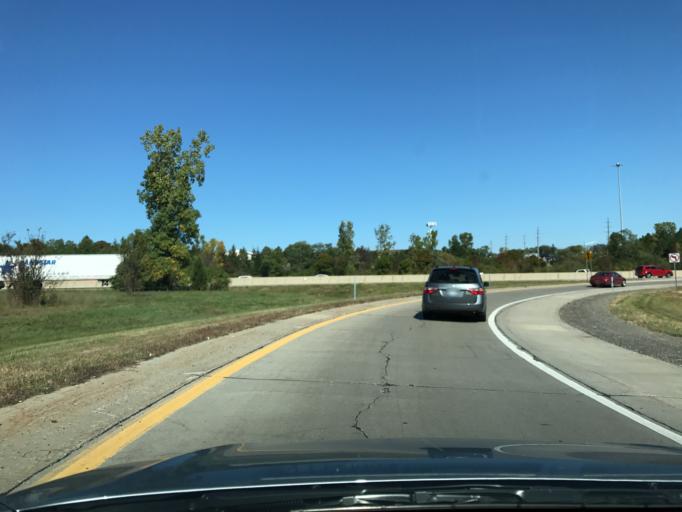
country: US
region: Michigan
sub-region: Oakland County
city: Farmington Hills
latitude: 42.4951
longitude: -83.3603
